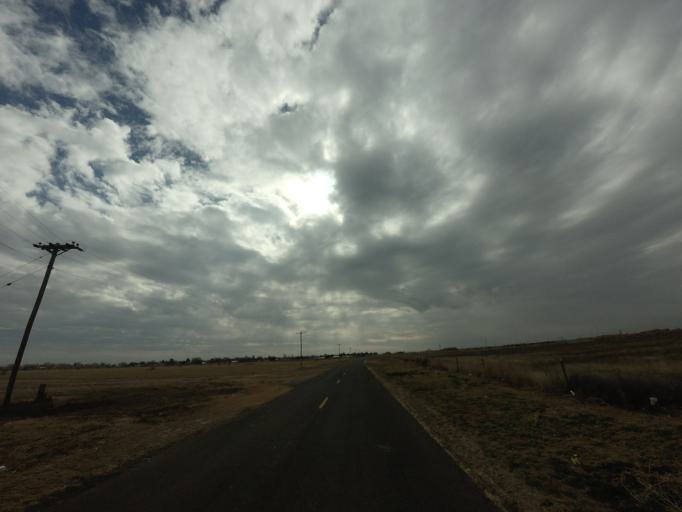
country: US
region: New Mexico
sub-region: Curry County
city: Clovis
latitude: 34.3873
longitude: -103.2054
